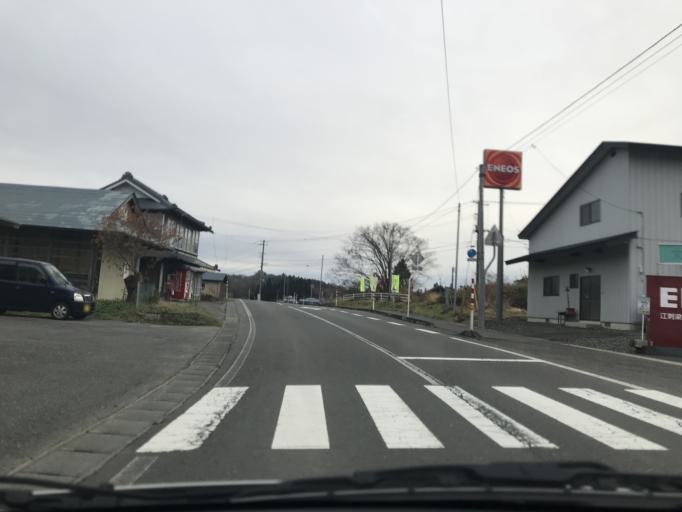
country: JP
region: Iwate
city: Kitakami
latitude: 39.2772
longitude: 141.2660
